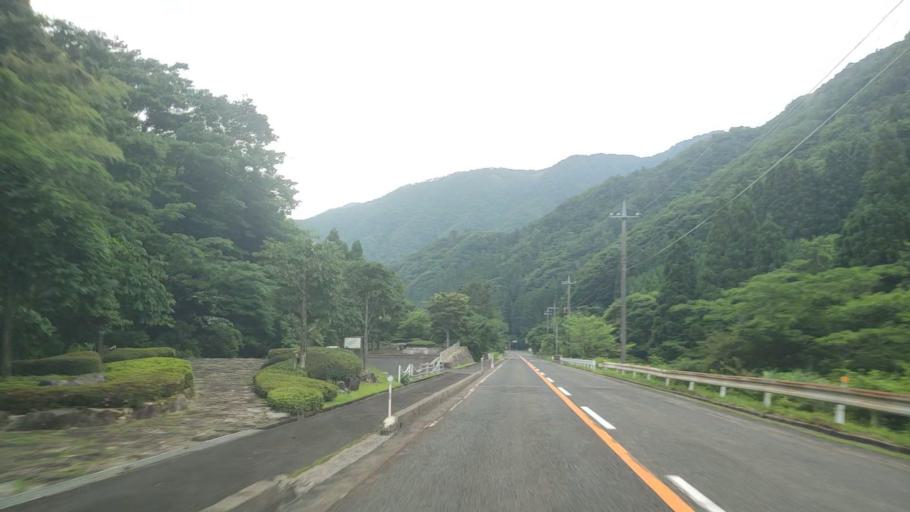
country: JP
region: Tottori
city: Kurayoshi
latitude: 35.3158
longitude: 133.9004
